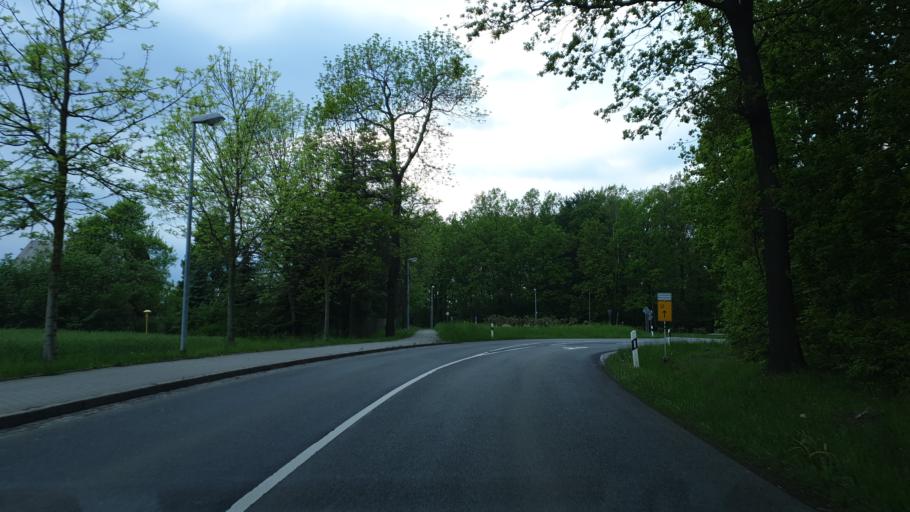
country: DE
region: Saxony
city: Oelsnitz
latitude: 50.7170
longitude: 12.7218
